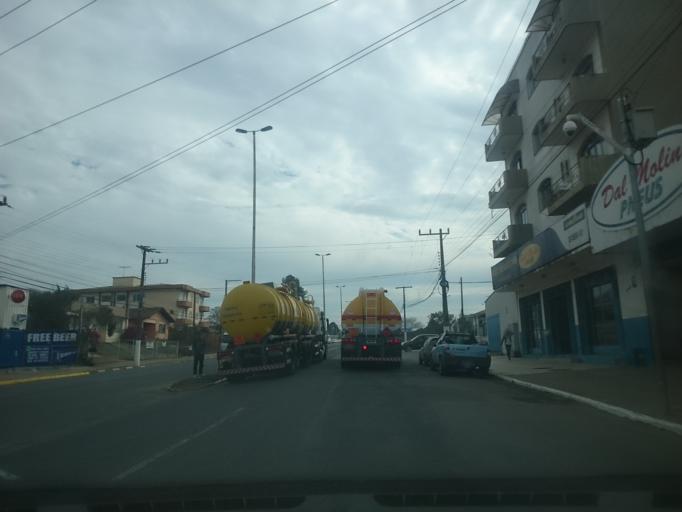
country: BR
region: Santa Catarina
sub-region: Lages
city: Lages
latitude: -27.7945
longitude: -50.3064
